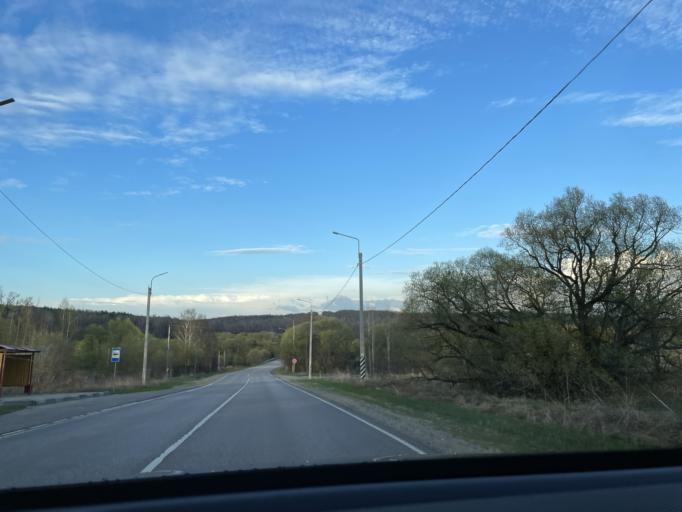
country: RU
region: Tula
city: Novogurovskiy
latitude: 54.5223
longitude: 37.2585
